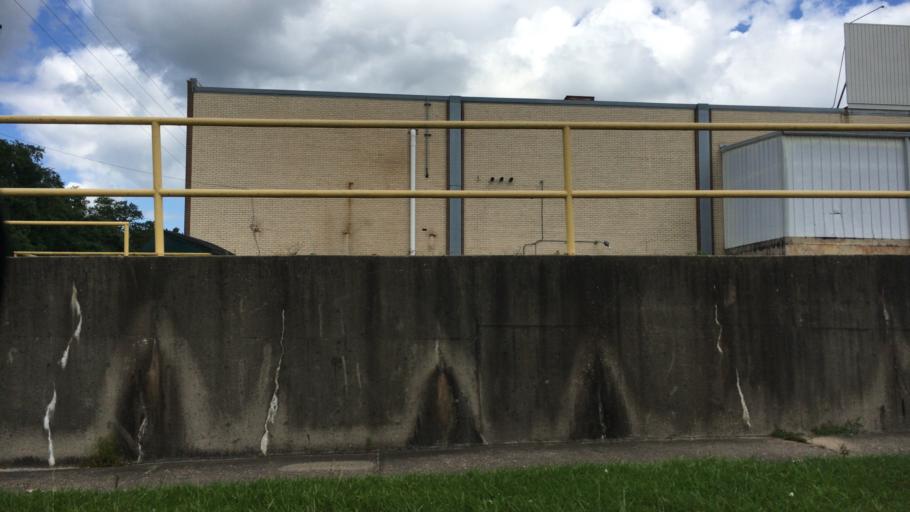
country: US
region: Louisiana
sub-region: Lincoln Parish
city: Ruston
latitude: 32.5266
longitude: -92.6394
